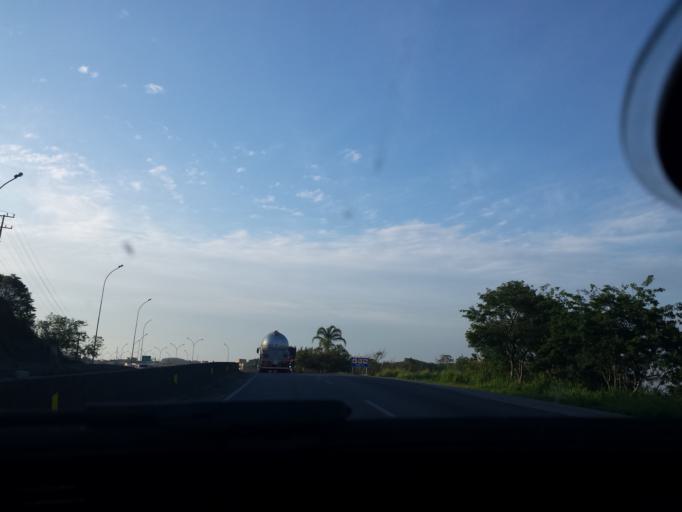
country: BR
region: Santa Catarina
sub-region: Imbituba
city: Imbituba
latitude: -28.2598
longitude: -48.7046
